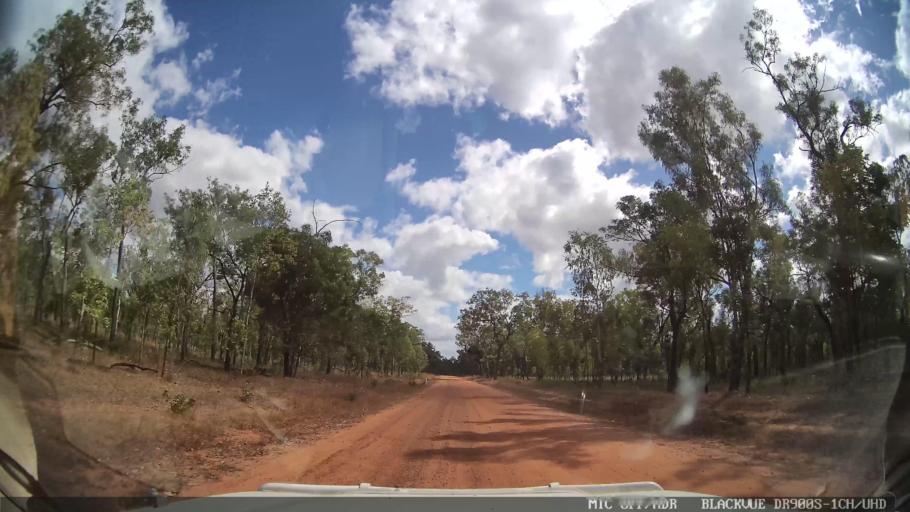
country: AU
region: Queensland
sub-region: Cook
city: Cooktown
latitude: -15.3518
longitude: 144.4635
